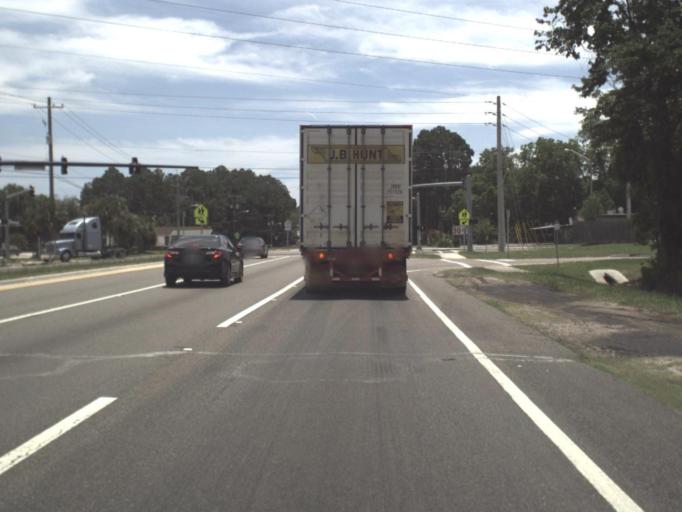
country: US
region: Florida
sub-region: Duval County
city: Jacksonville
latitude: 30.3876
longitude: -81.7338
